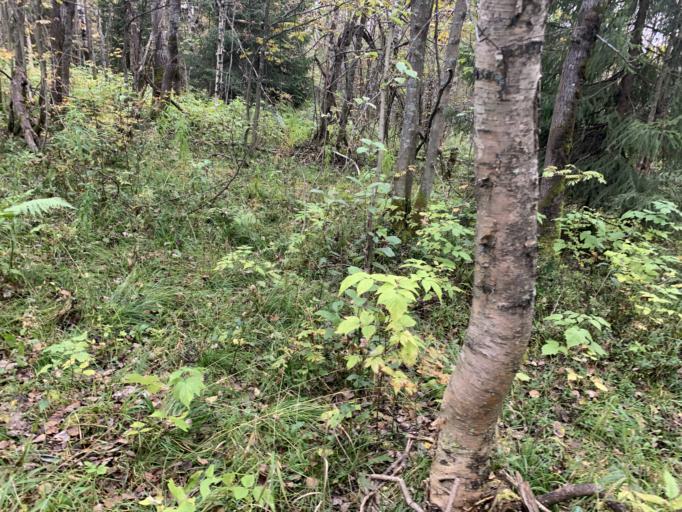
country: RU
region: Perm
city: Gubakha
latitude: 58.8466
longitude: 57.5799
